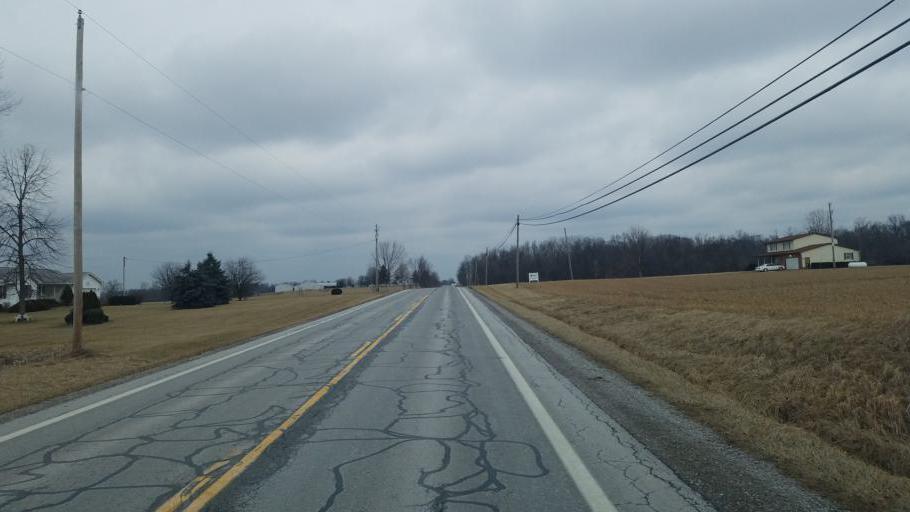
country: US
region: Ohio
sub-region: Morrow County
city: Mount Gilead
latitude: 40.6334
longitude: -82.8226
